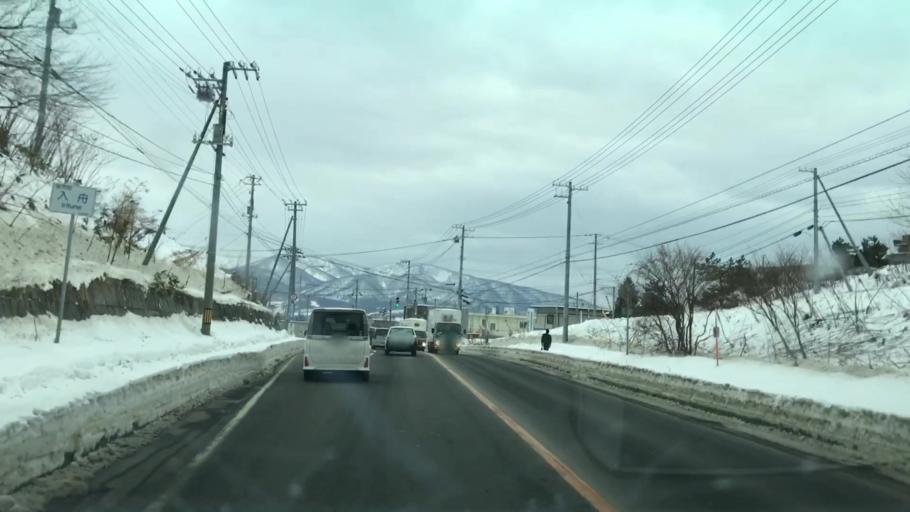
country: JP
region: Hokkaido
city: Yoichi
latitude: 43.1965
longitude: 140.7847
